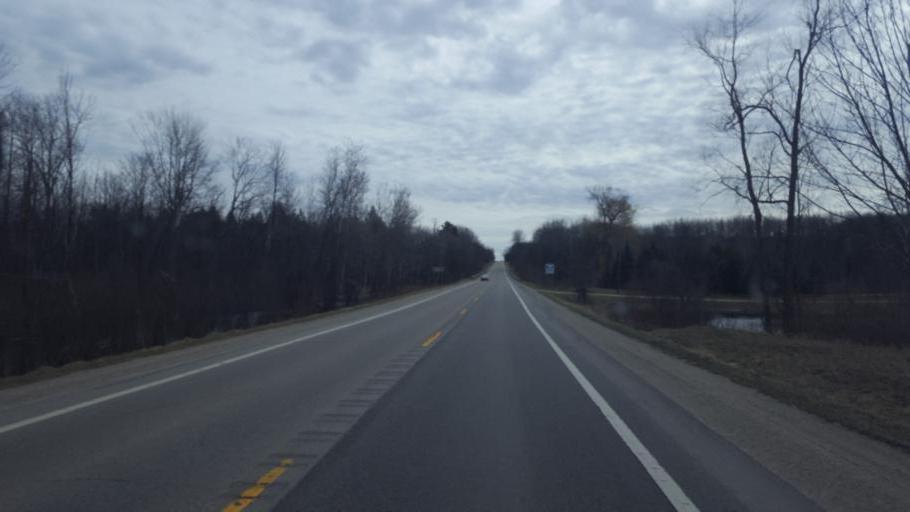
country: US
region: Michigan
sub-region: Isabella County
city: Lake Isabella
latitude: 43.6897
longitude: -85.1466
